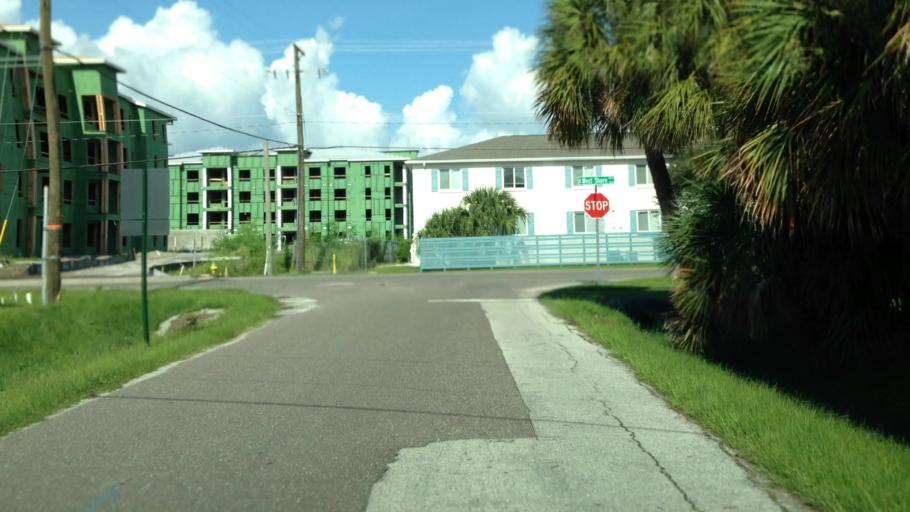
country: US
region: Florida
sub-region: Hillsborough County
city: Tampa
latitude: 27.8877
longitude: -82.5265
